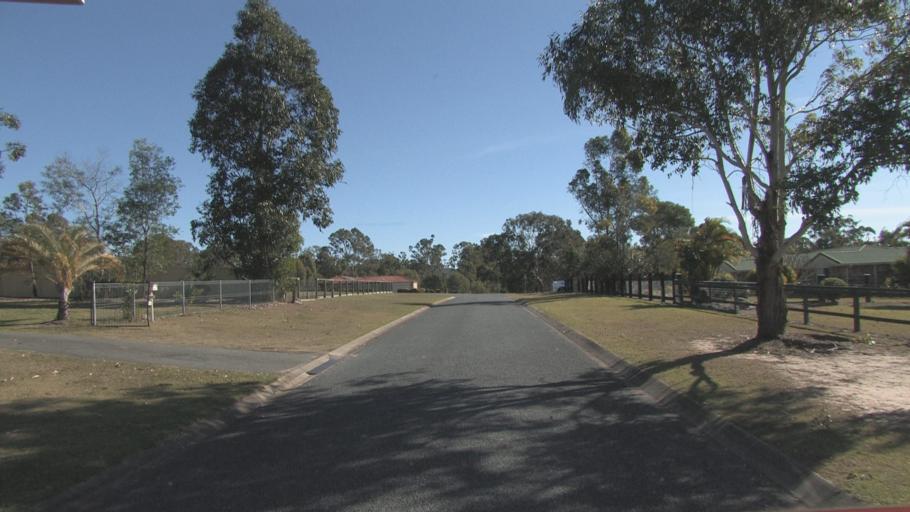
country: AU
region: Queensland
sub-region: Ipswich
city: Springfield Lakes
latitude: -27.7285
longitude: 152.9432
